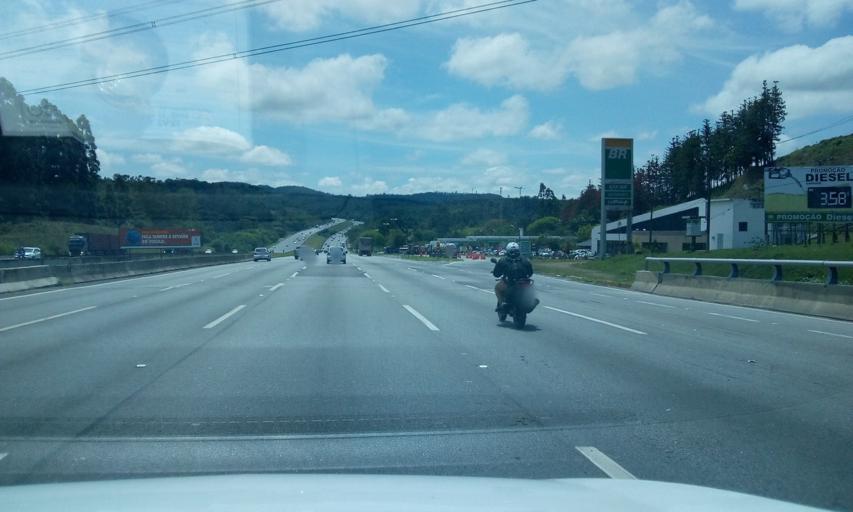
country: BR
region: Sao Paulo
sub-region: Caieiras
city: Caieiras
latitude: -23.3974
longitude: -46.7680
